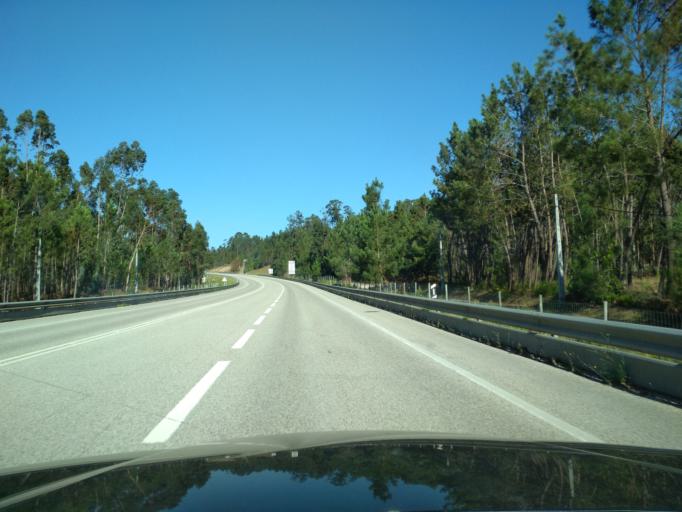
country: PT
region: Leiria
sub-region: Pombal
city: Lourical
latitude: 39.9865
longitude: -8.7663
